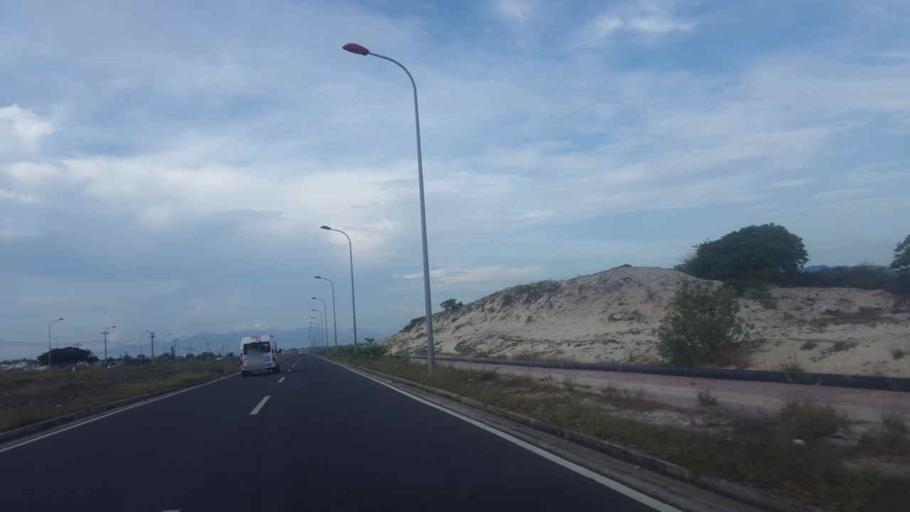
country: VN
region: Khanh Hoa
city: Cam Lam
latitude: 12.0099
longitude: 109.2109
